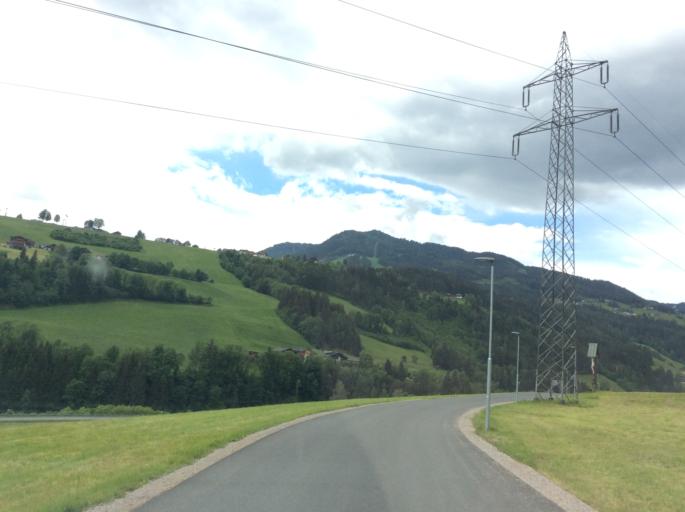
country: AT
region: Styria
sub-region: Politischer Bezirk Liezen
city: Schladming
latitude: 47.3939
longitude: 13.6698
